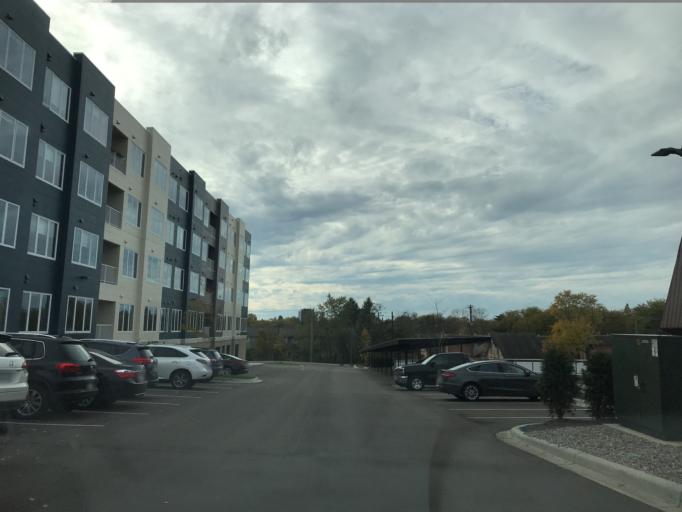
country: US
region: Michigan
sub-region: Washtenaw County
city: Ann Arbor
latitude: 42.2505
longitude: -83.7235
